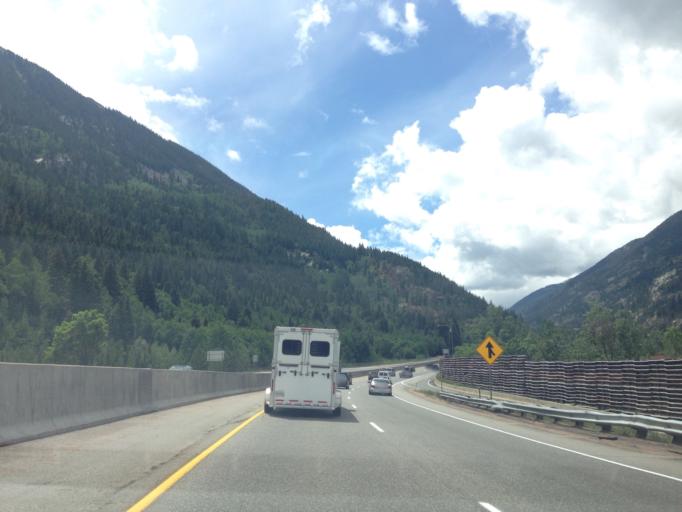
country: US
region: Colorado
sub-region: Clear Creek County
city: Georgetown
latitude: 39.6944
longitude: -105.7272
